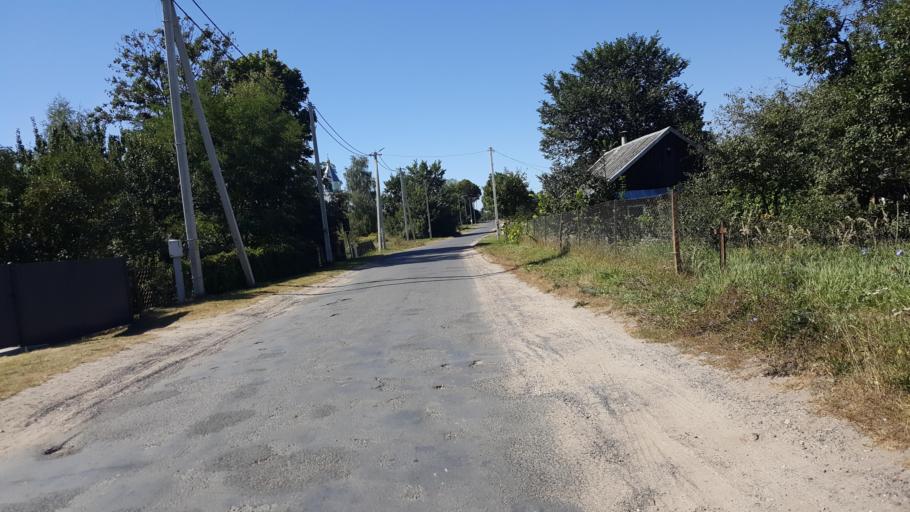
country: BY
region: Brest
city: Vysokaye
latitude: 52.2209
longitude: 23.4237
